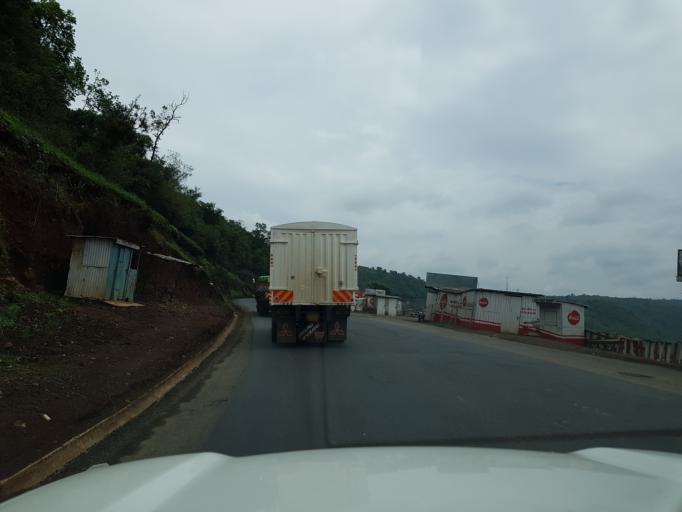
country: KE
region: Kiambu
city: Limuru
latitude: -1.0580
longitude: 36.6032
